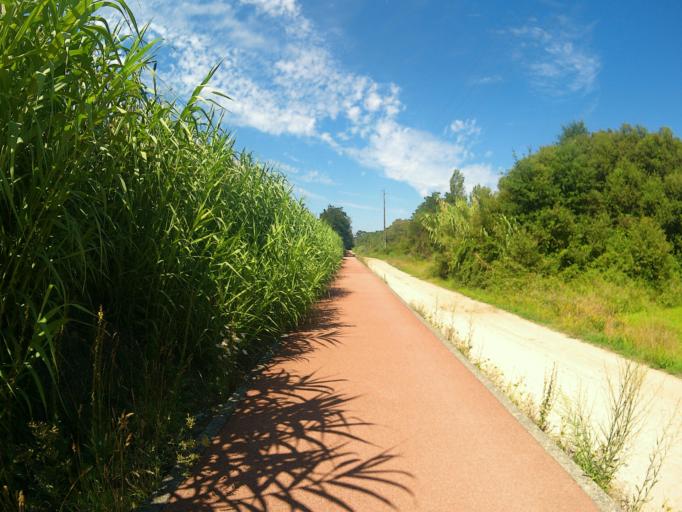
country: PT
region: Viana do Castelo
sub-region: Valenca
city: Valenca
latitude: 42.0060
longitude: -8.6560
